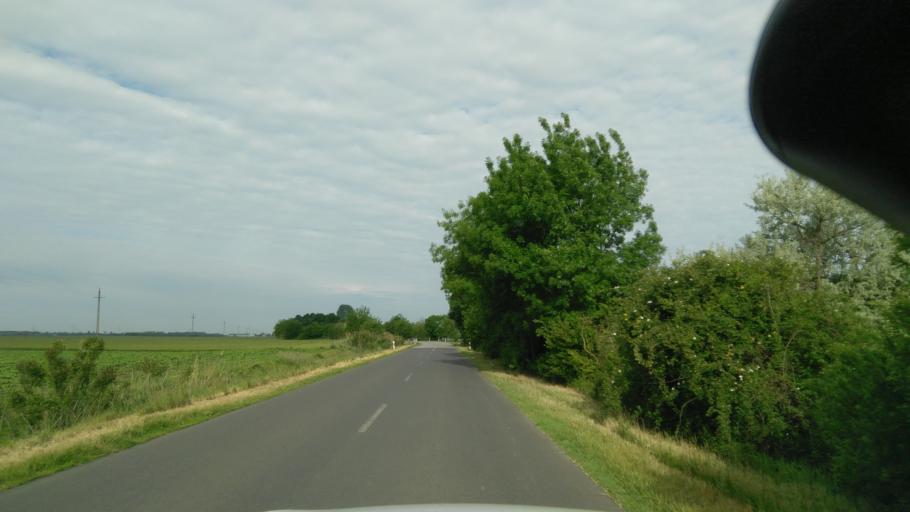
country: HU
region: Bekes
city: Ketegyhaza
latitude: 46.5394
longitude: 21.1498
